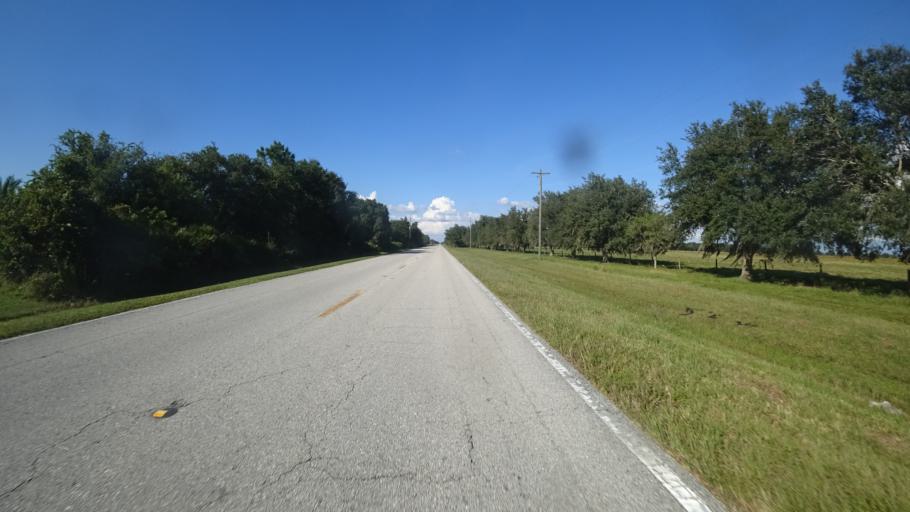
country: US
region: Florida
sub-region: Sarasota County
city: The Meadows
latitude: 27.4203
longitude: -82.3037
